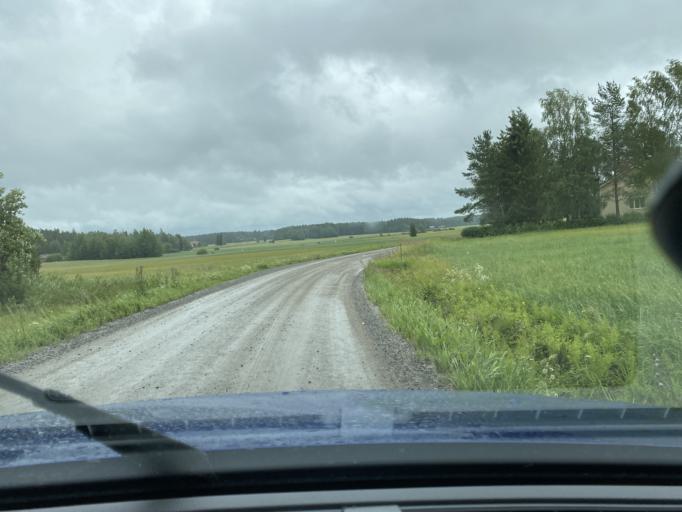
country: FI
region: Pirkanmaa
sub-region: Lounais-Pirkanmaa
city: Punkalaidun
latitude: 61.1485
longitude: 23.2148
